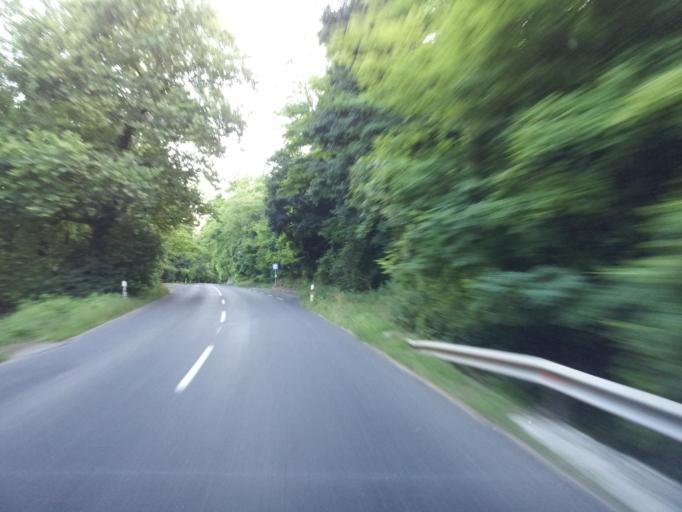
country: HU
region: Veszprem
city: Zanka
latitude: 46.9413
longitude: 17.5876
